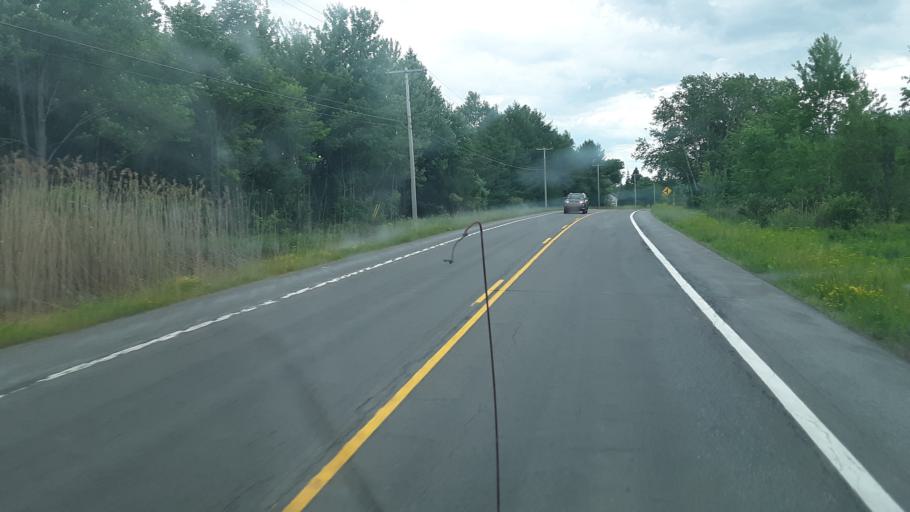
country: US
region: New York
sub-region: Oneida County
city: Rome
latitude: 43.3392
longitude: -75.4759
